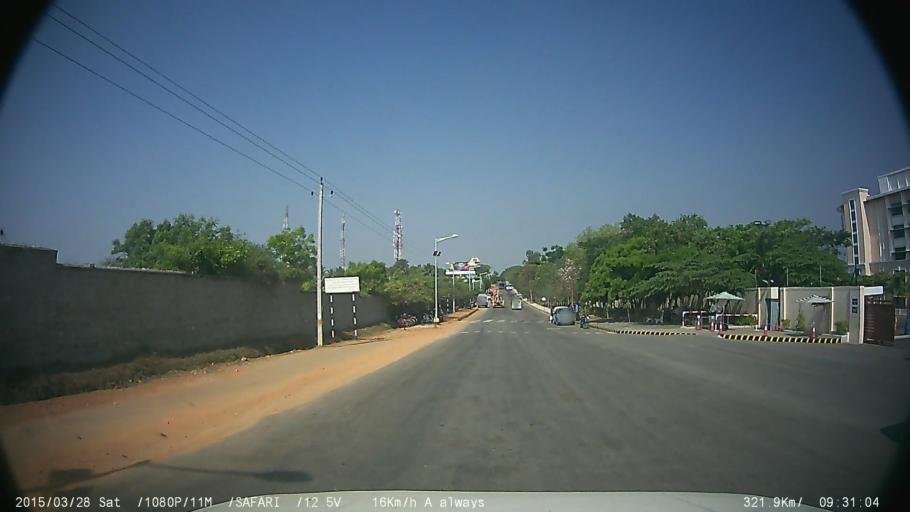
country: IN
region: Karnataka
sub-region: Mysore
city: Mysore
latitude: 12.3578
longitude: 76.6004
